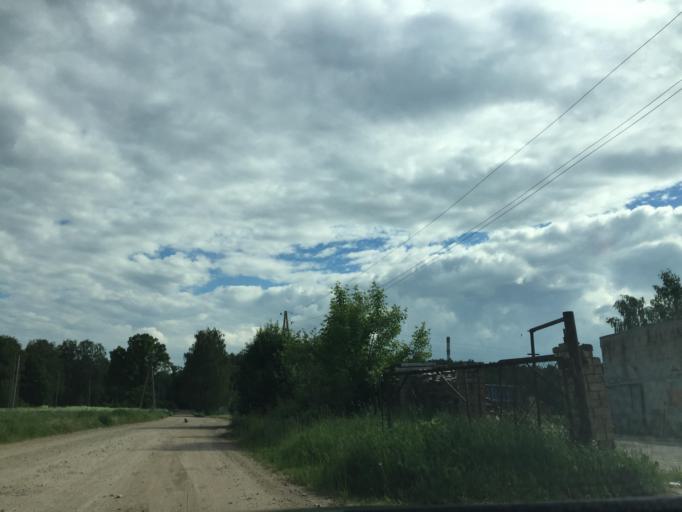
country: LV
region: Stopini
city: Ulbroka
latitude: 56.9317
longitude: 24.2888
